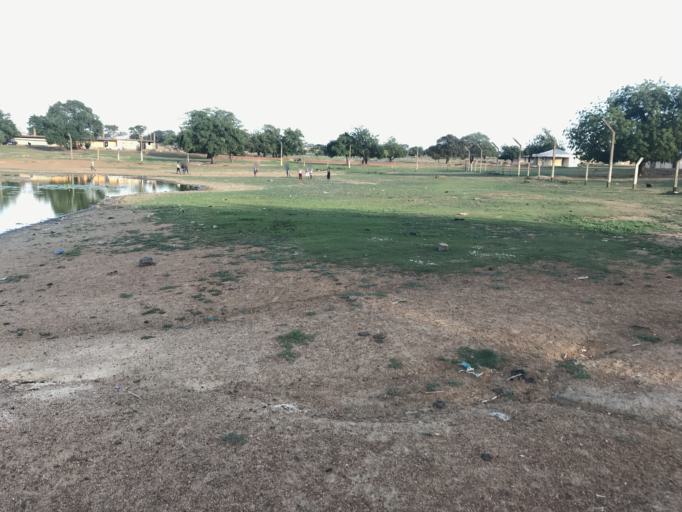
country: GH
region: Upper East
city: Navrongo
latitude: 10.9845
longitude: -1.1094
